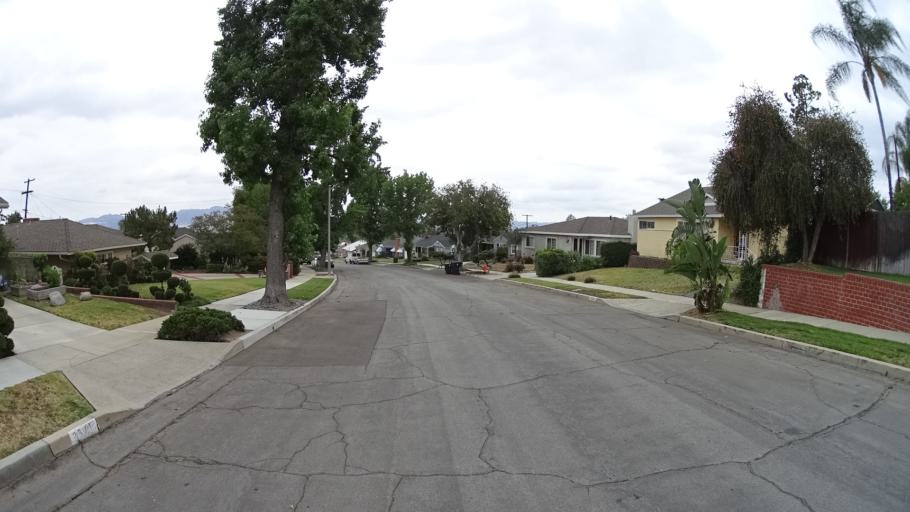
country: US
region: California
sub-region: Los Angeles County
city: Burbank
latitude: 34.2050
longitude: -118.3303
